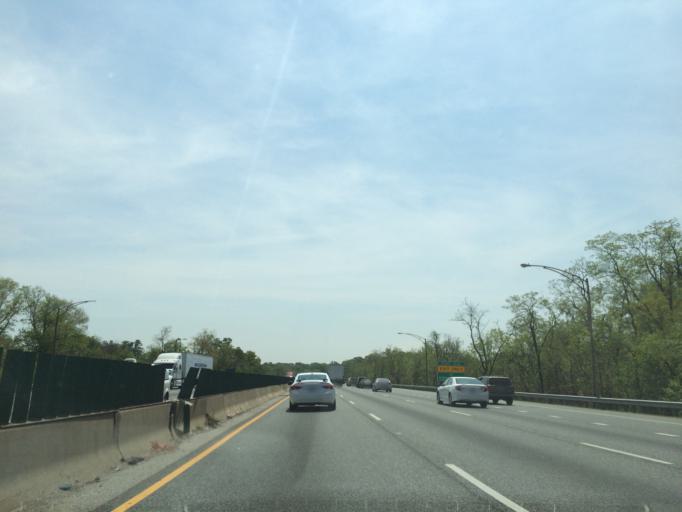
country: US
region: Maryland
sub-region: Baltimore County
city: Catonsville
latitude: 39.2840
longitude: -76.7351
